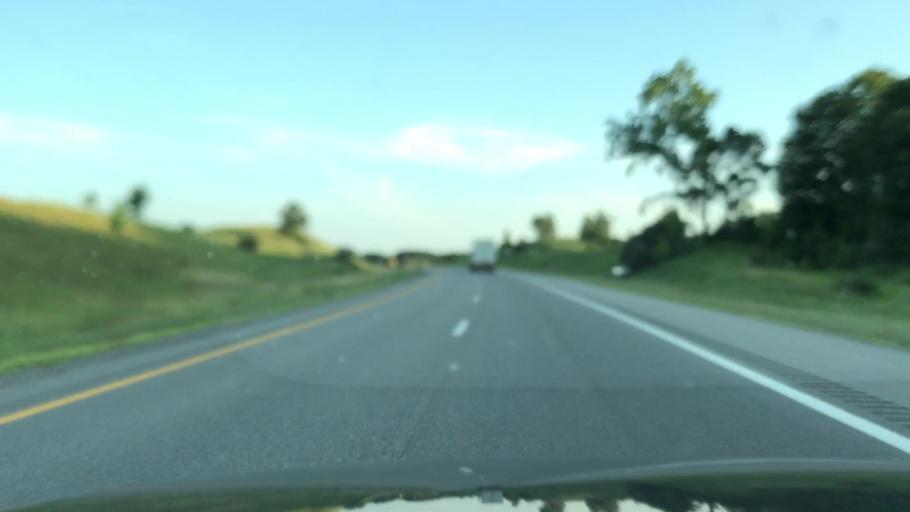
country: US
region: Michigan
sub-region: Osceola County
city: Reed City
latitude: 43.8644
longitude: -85.5354
